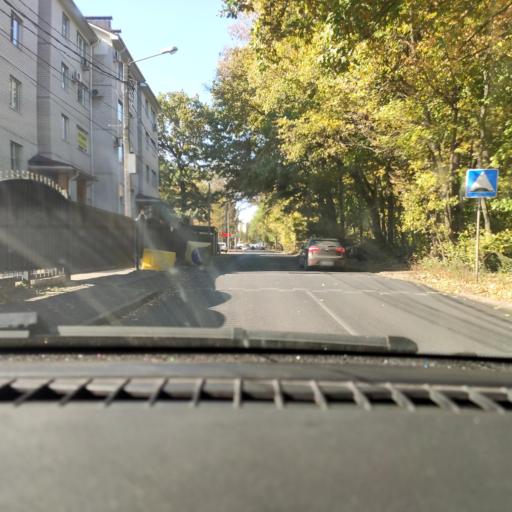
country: RU
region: Voronezj
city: Voronezh
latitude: 51.7248
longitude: 39.2175
